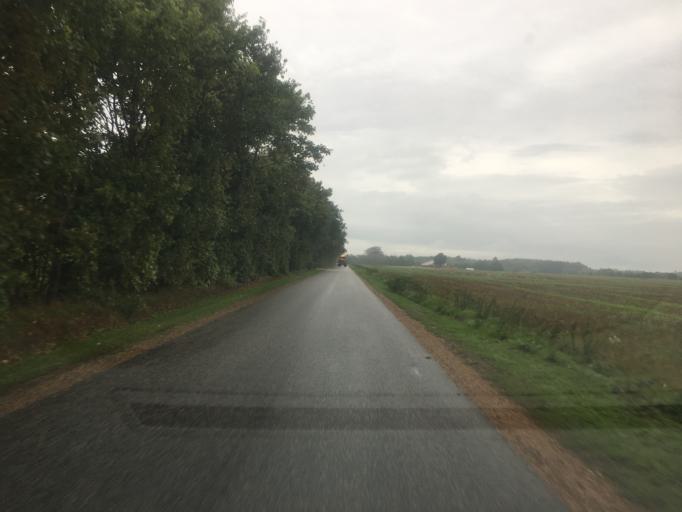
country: DK
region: South Denmark
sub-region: Tonder Kommune
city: Logumkloster
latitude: 55.0221
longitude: 9.0351
